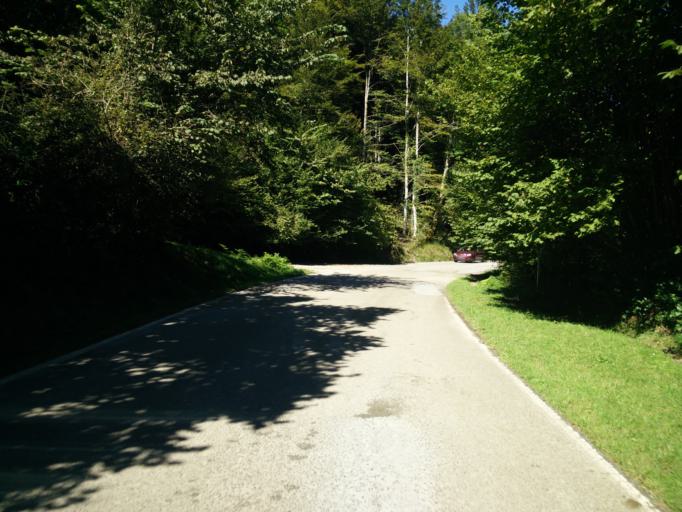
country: ES
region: Cantabria
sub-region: Provincia de Cantabria
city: Ruente
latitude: 43.1247
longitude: -4.2969
